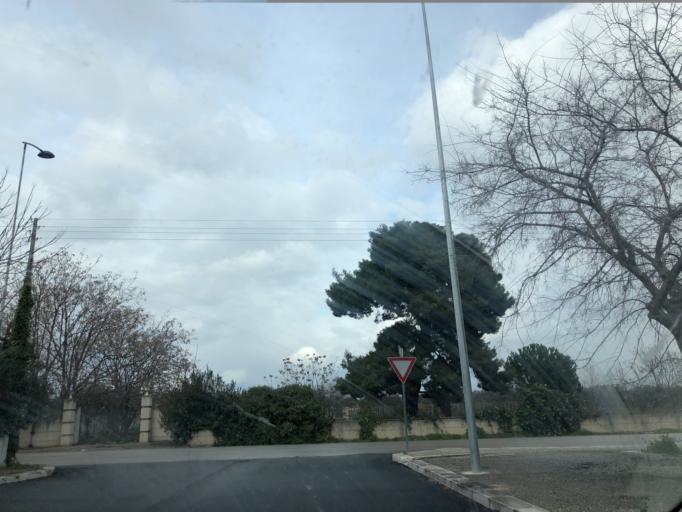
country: IT
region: Apulia
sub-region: Provincia di Foggia
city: Lucera
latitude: 41.5016
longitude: 15.3537
